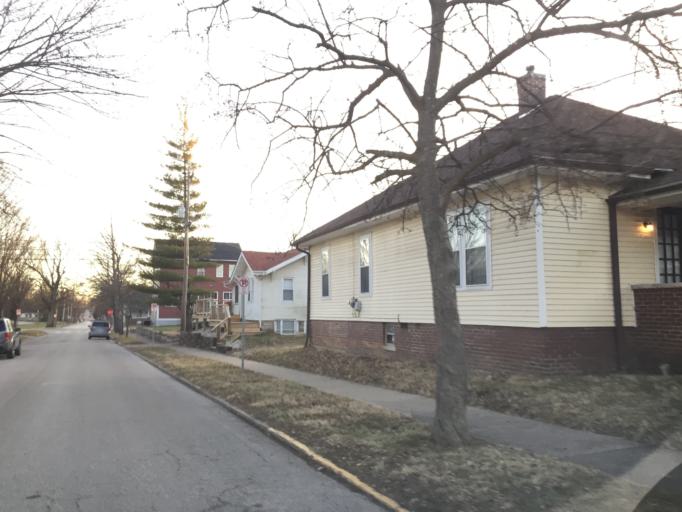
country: US
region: Indiana
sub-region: Monroe County
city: Bloomington
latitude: 39.1726
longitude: -86.5283
